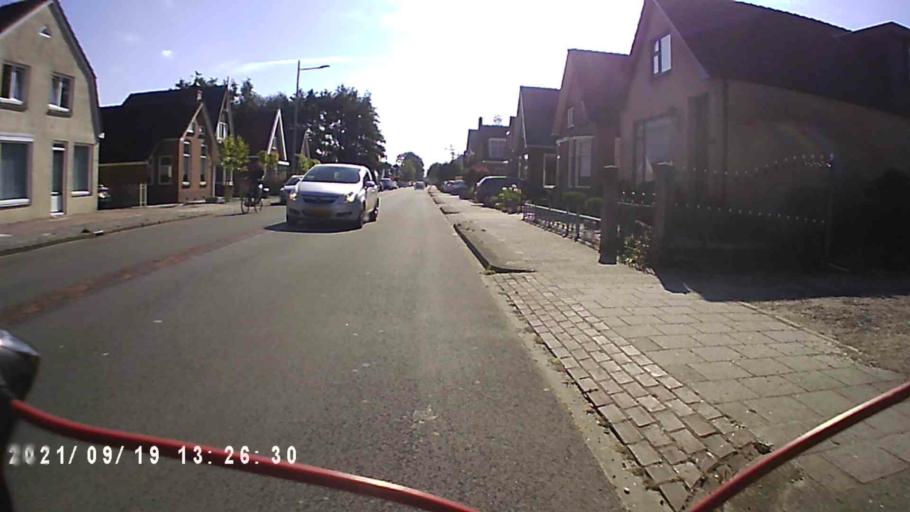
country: NL
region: Groningen
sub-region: Gemeente  Oldambt
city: Winschoten
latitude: 53.1534
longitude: 7.0169
